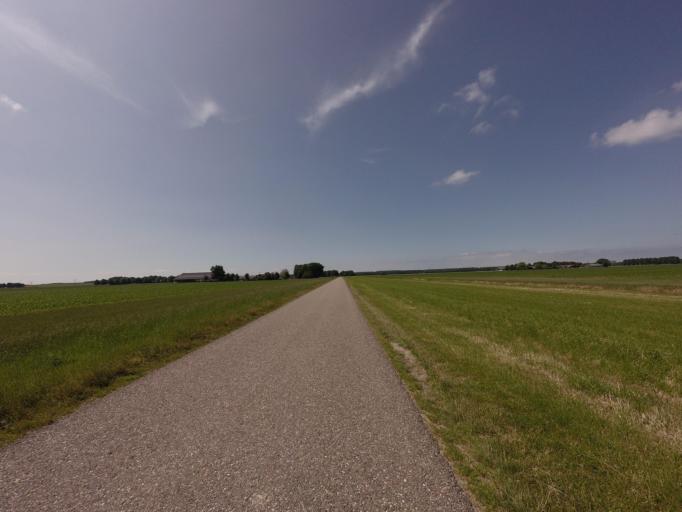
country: NL
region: Flevoland
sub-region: Gemeente Lelystad
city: Lelystad
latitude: 52.4377
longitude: 5.4651
